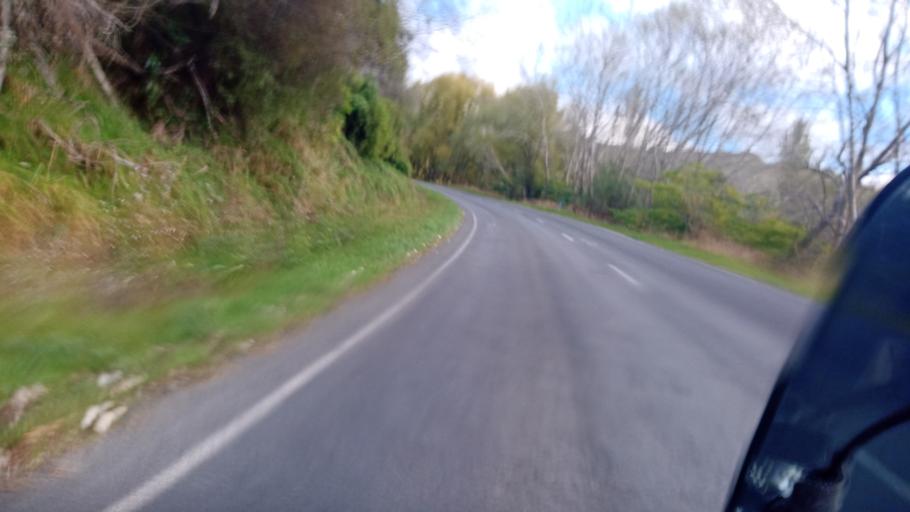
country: NZ
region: Gisborne
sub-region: Gisborne District
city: Gisborne
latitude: -38.5914
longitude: 177.7687
